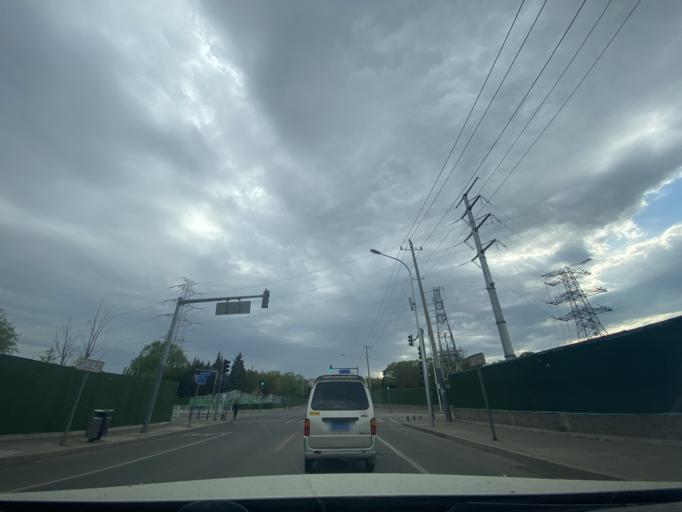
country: CN
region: Beijing
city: Haidian
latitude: 39.9722
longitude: 116.2828
